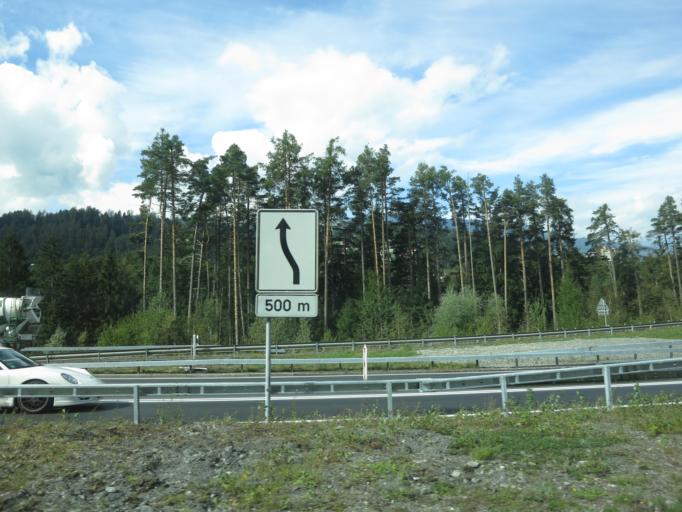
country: CH
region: Grisons
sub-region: Hinterrhein District
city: Thusis
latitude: 46.6959
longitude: 9.4456
